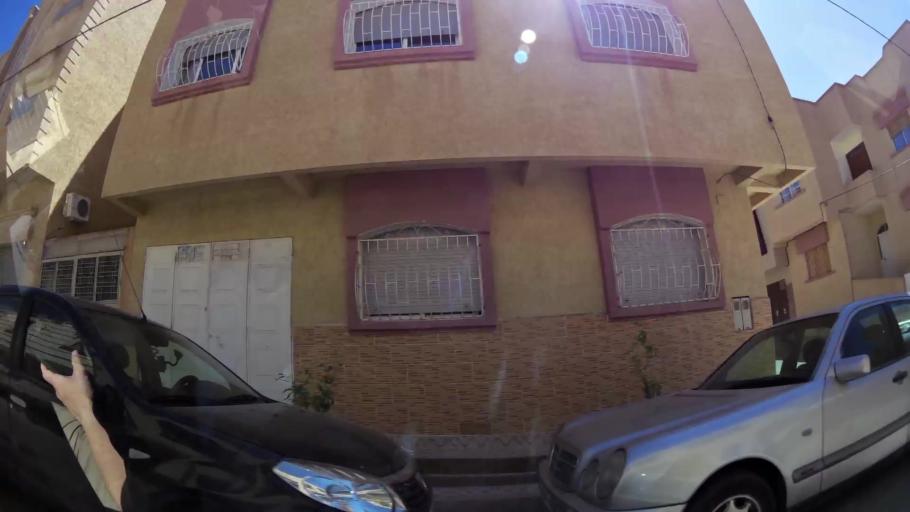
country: MA
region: Oriental
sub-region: Oujda-Angad
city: Oujda
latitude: 34.6480
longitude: -1.9097
